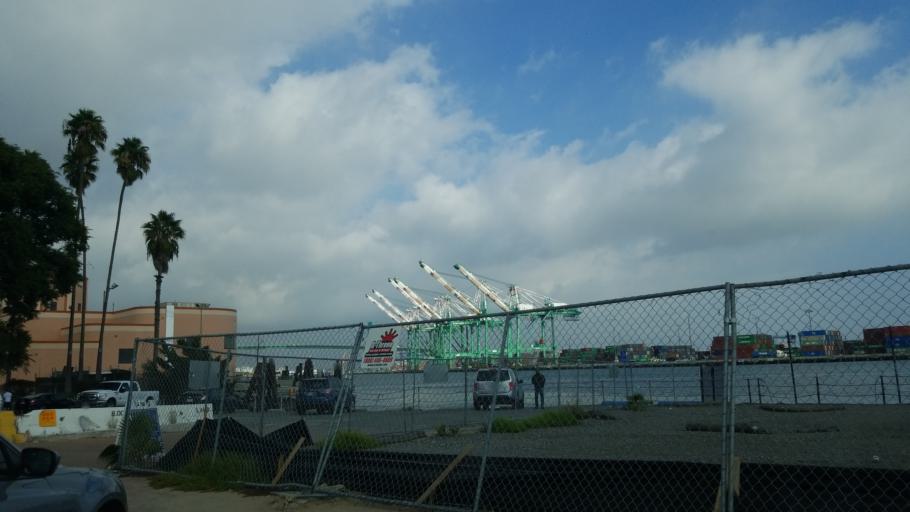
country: US
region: California
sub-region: Los Angeles County
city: San Pedro
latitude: 33.7377
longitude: -118.2790
